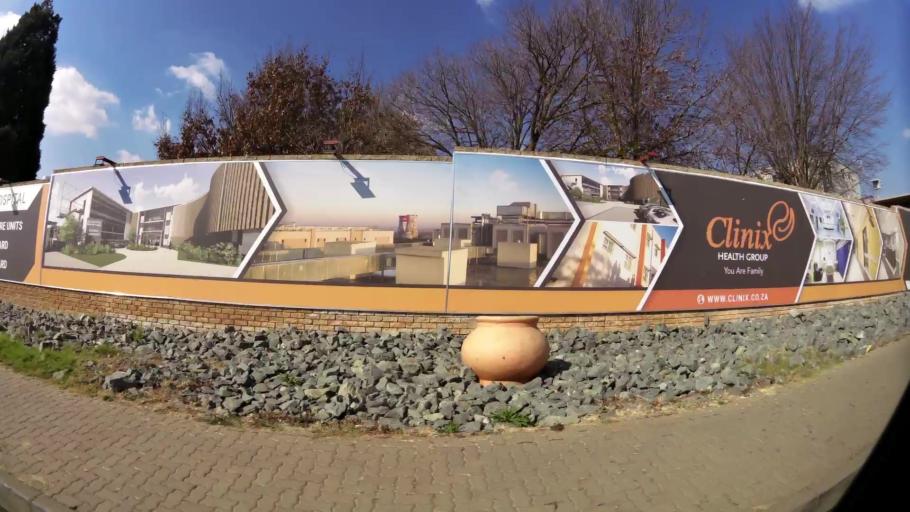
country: ZA
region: Gauteng
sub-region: City of Johannesburg Metropolitan Municipality
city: Soweto
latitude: -26.2582
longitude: 27.9348
